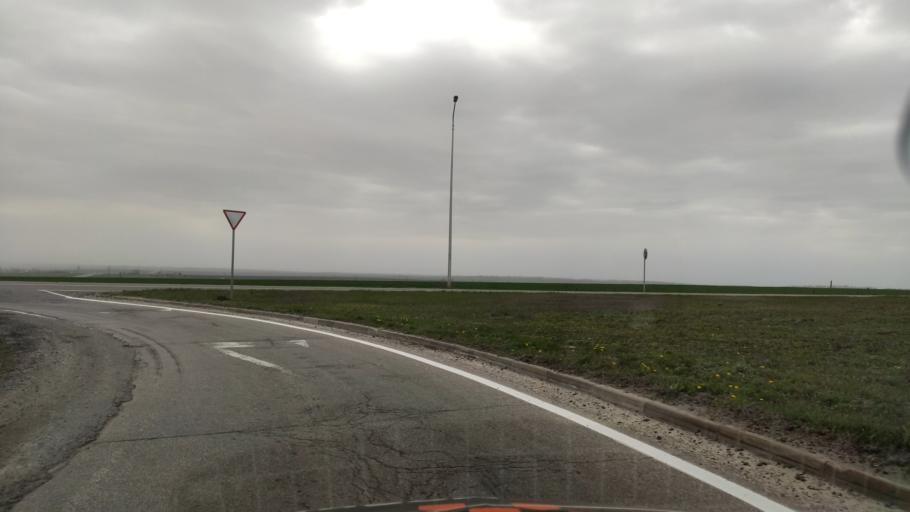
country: RU
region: Belgorod
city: Staryy Oskol
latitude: 51.3288
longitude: 37.7412
